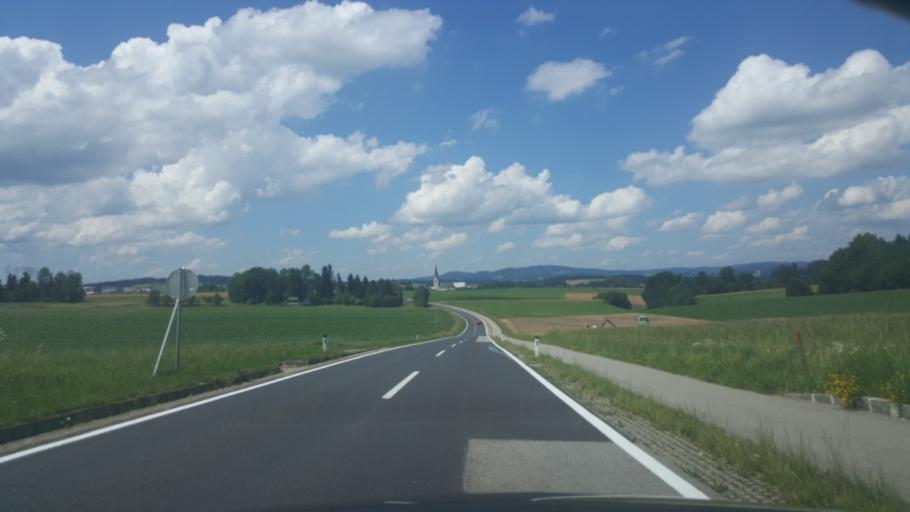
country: AT
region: Upper Austria
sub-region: Politischer Bezirk Vocklabruck
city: Gampern
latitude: 47.9779
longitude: 13.5607
